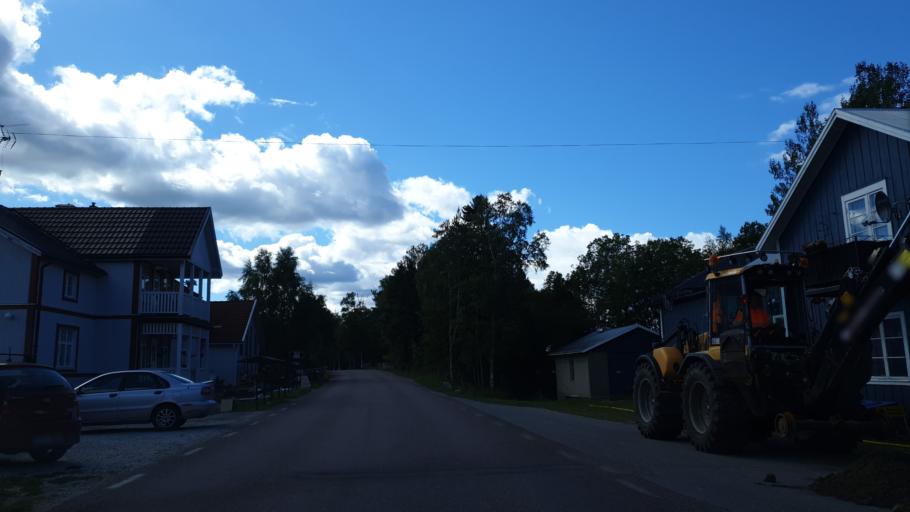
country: SE
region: Gaevleborg
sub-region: Nordanstigs Kommun
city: Bergsjoe
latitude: 62.0471
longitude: 17.2509
